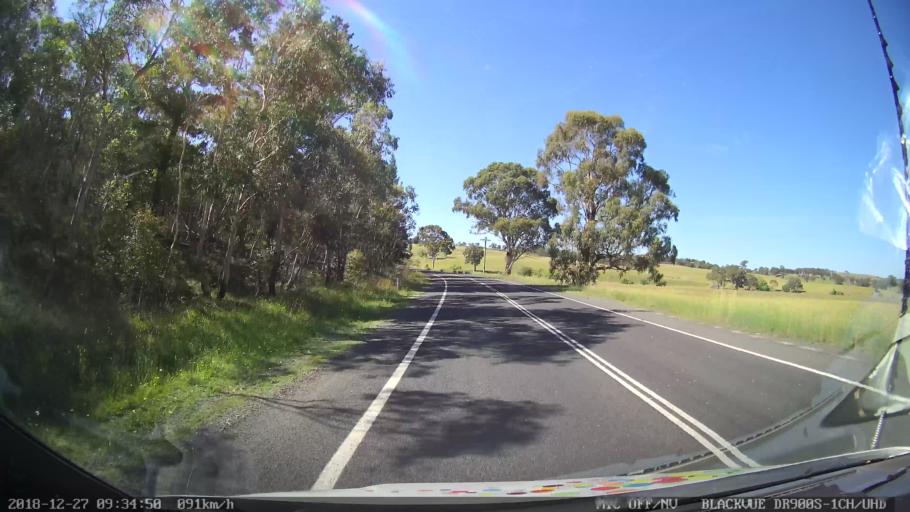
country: AU
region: New South Wales
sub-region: Lithgow
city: Portland
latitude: -33.2313
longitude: 150.0261
